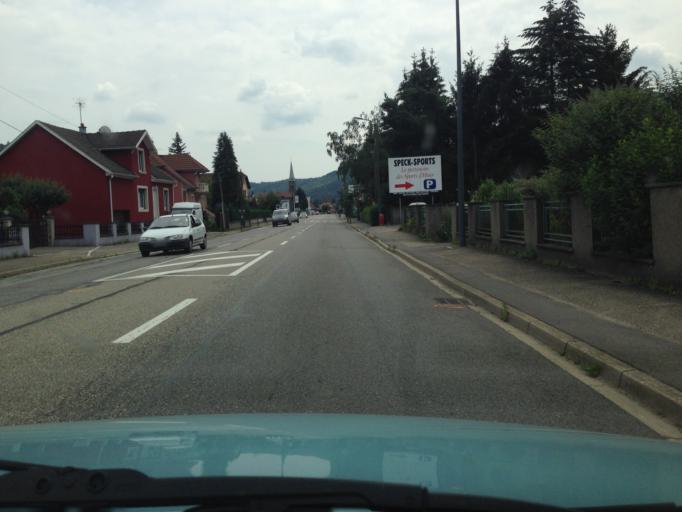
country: FR
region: Alsace
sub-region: Departement du Haut-Rhin
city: Bitschwiller-les-Thann
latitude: 47.8355
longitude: 7.0764
